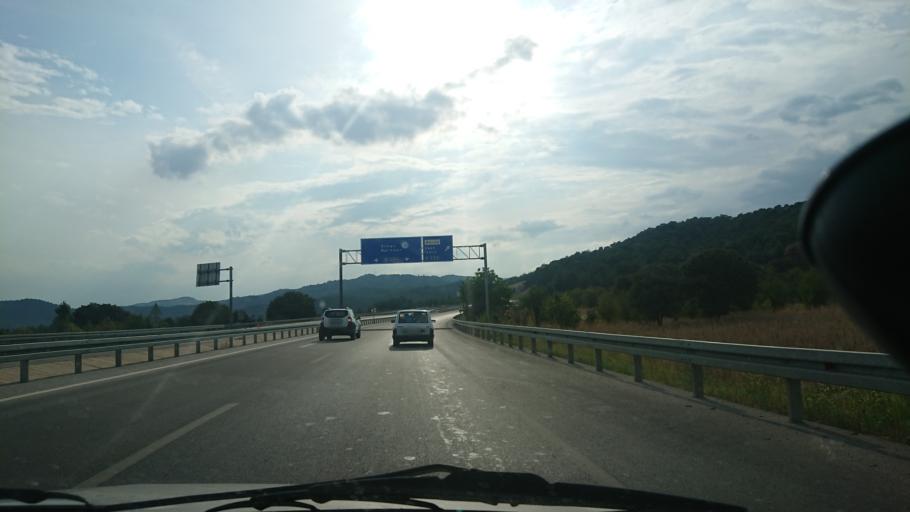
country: TR
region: Kuetahya
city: Gediz
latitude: 38.9359
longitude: 29.3137
